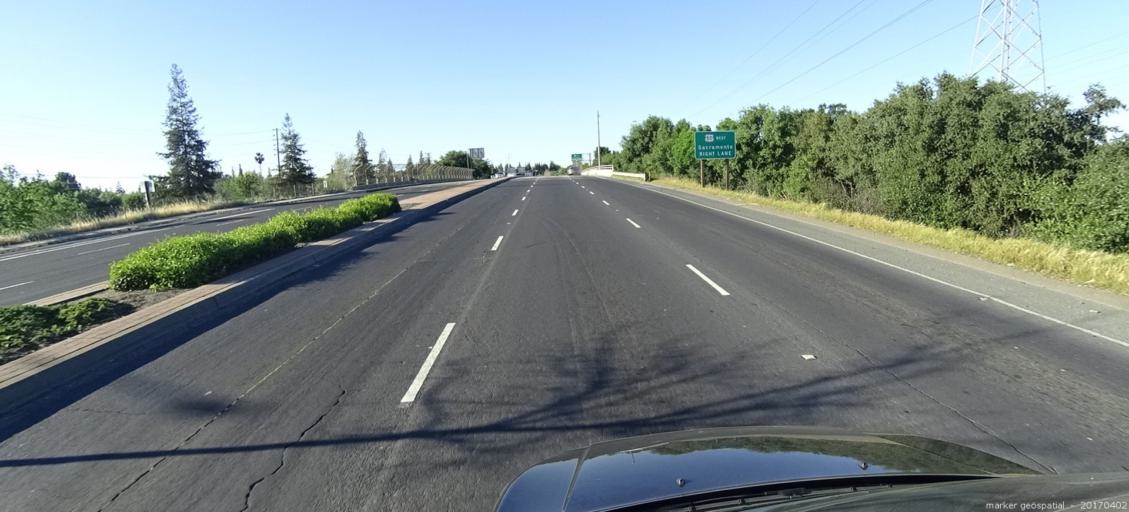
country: US
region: California
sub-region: Sacramento County
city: Rosemont
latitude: 38.5527
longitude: -121.4093
